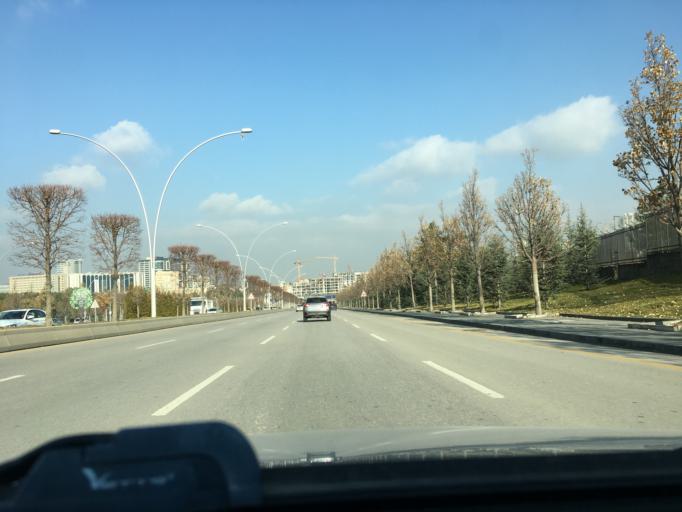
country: TR
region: Ankara
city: Ankara
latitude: 39.9035
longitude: 32.7881
